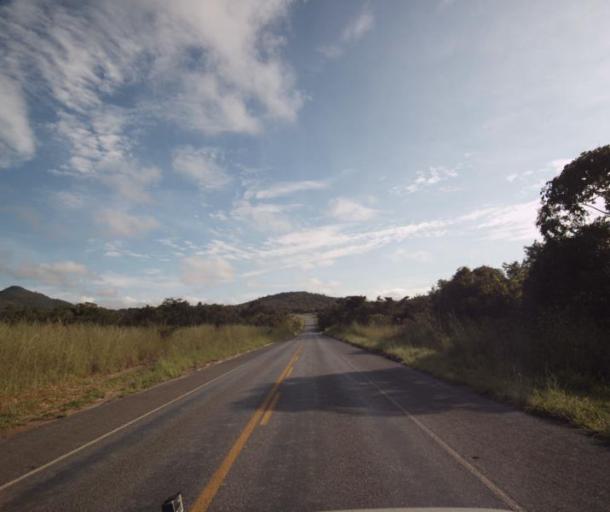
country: BR
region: Goias
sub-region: Pirenopolis
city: Pirenopolis
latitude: -15.5418
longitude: -48.6226
